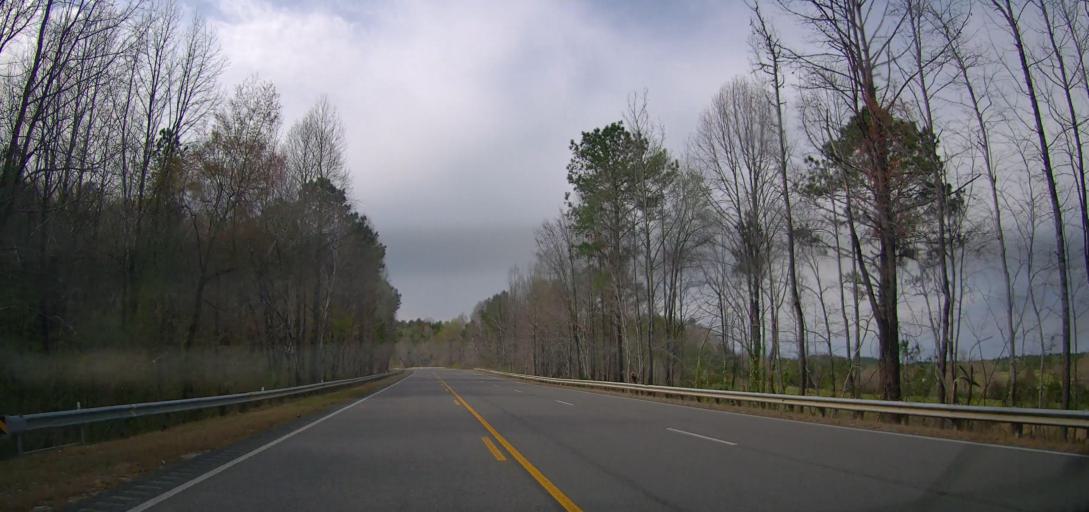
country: US
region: Alabama
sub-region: Walker County
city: Carbon Hill
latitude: 33.9146
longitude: -87.5645
